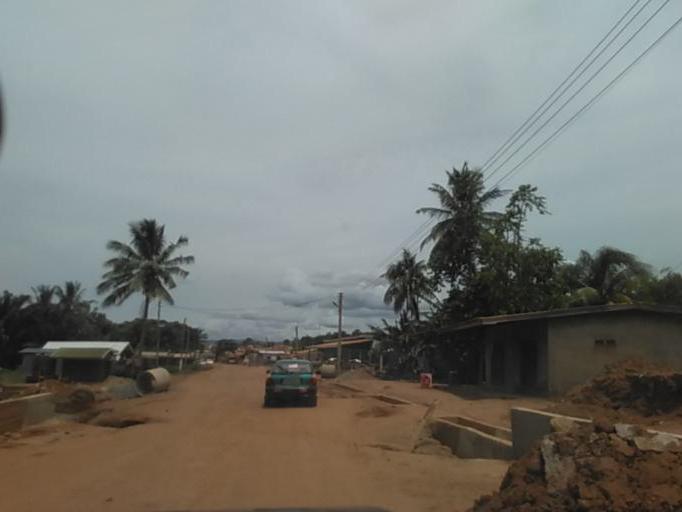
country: GH
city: Akropong
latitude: 6.1346
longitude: 0.0035
